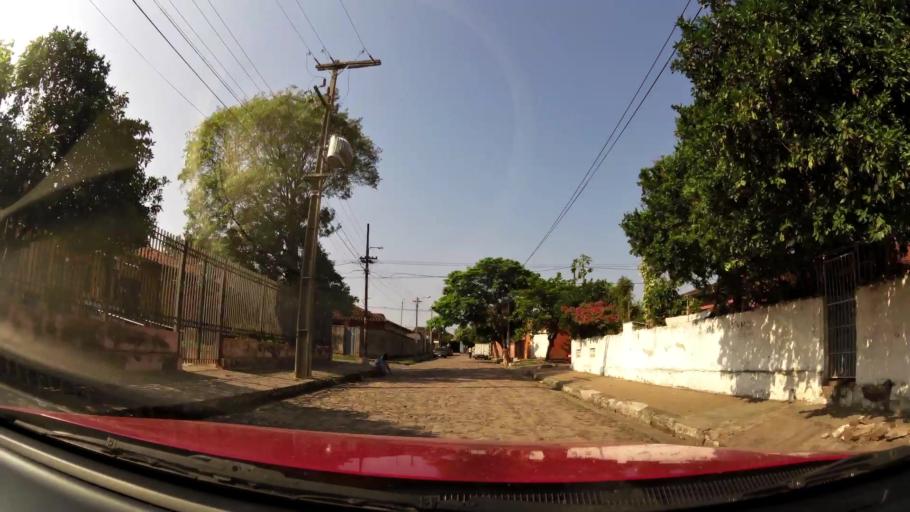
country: PY
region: Asuncion
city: Asuncion
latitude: -25.3182
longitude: -57.6379
